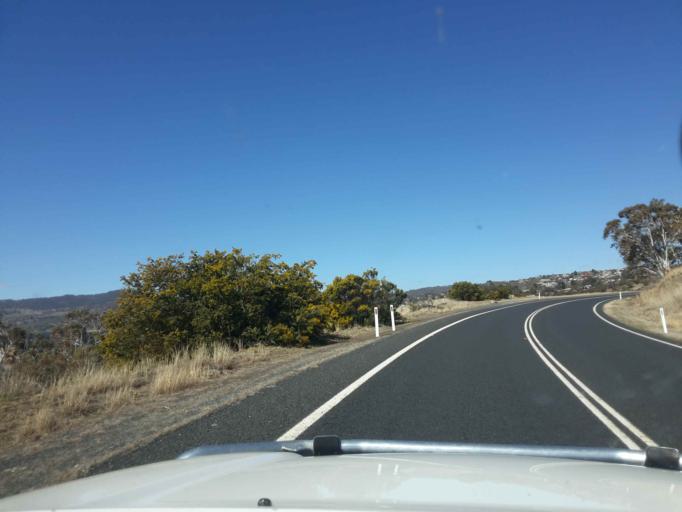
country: AU
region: New South Wales
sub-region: Snowy River
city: Jindabyne
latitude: -36.4050
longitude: 148.5996
